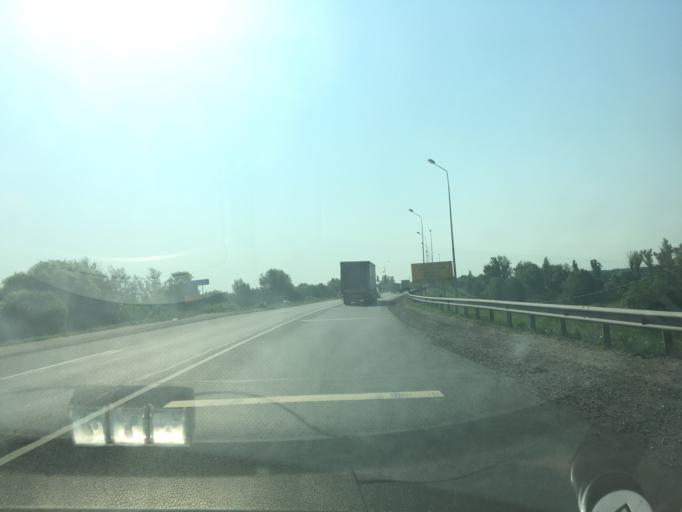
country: RU
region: Nizjnij Novgorod
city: Kstovo
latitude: 56.0995
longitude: 44.3069
